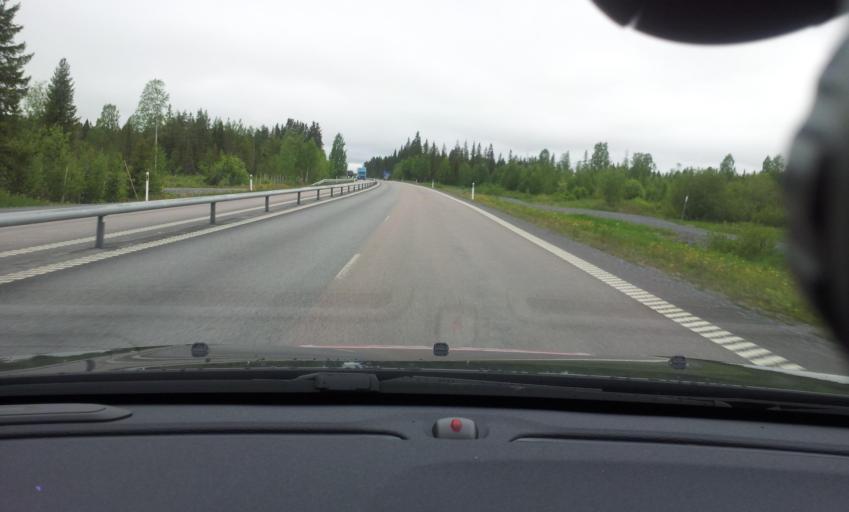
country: SE
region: Jaemtland
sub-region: OEstersunds Kommun
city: Ostersund
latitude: 63.2512
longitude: 14.5833
